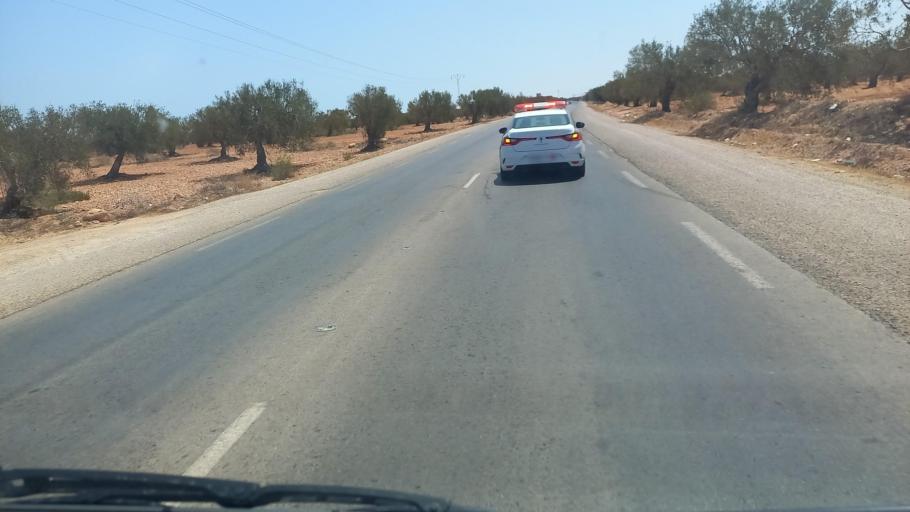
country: TN
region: Madanin
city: Zarzis
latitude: 33.5540
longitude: 11.0629
